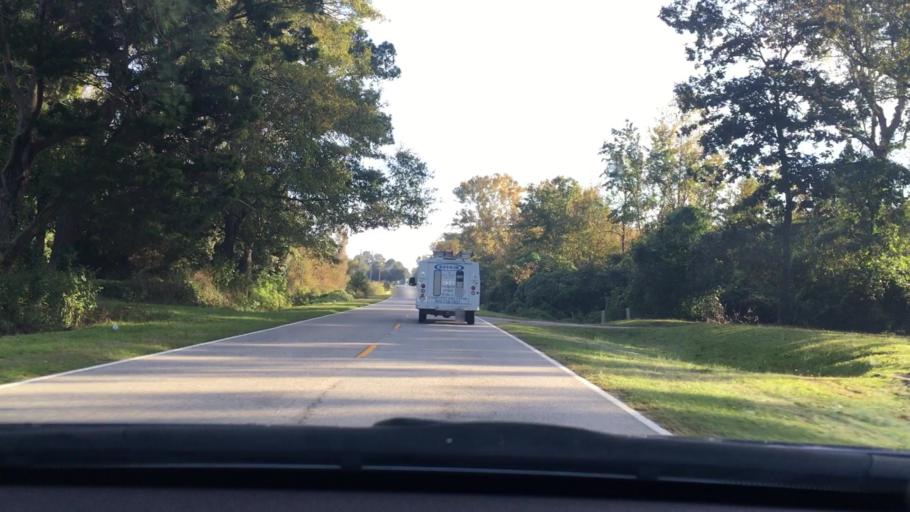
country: US
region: South Carolina
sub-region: Lee County
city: Bishopville
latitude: 34.1010
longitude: -80.1681
